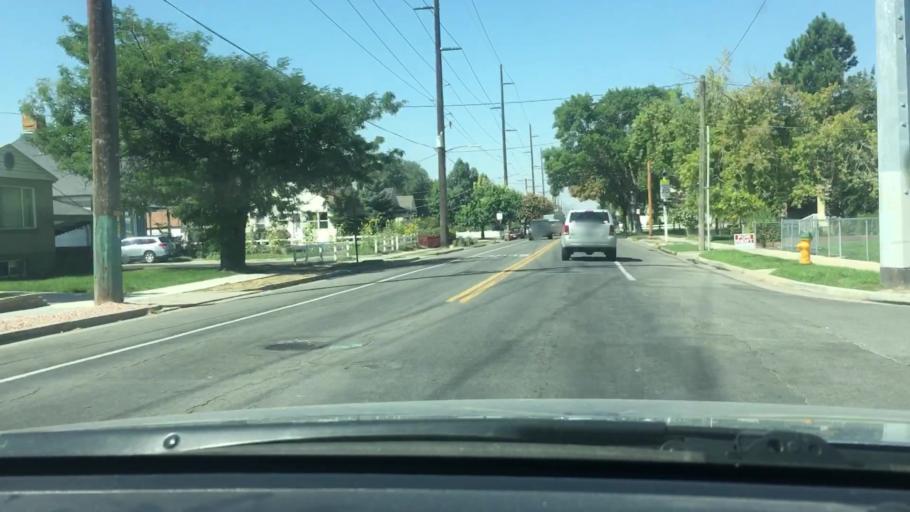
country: US
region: Utah
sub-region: Salt Lake County
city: South Salt Lake
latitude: 40.7127
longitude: -111.8668
